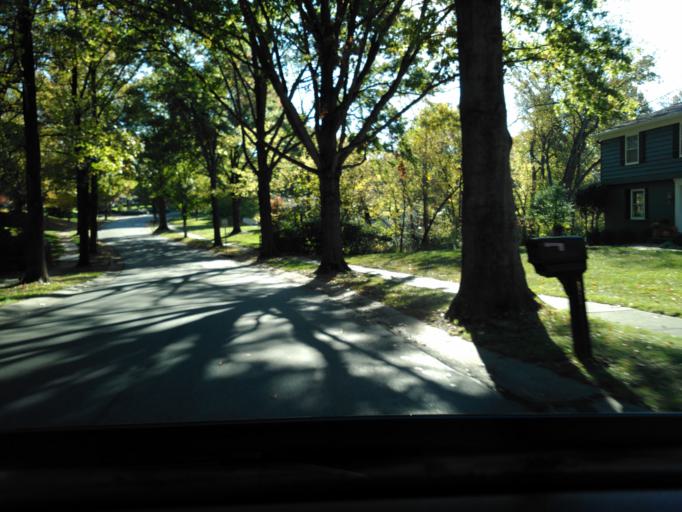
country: US
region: Missouri
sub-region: Saint Louis County
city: Town and Country
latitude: 38.6148
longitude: -90.4814
